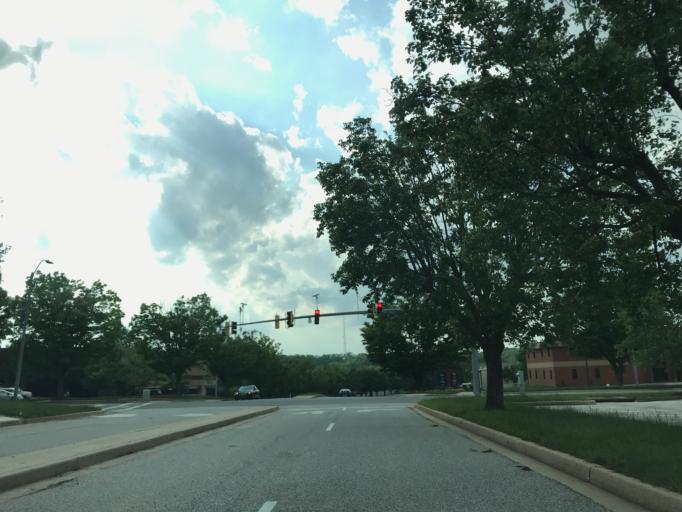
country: US
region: Maryland
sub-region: Harford County
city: North Bel Air
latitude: 39.5258
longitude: -76.3599
